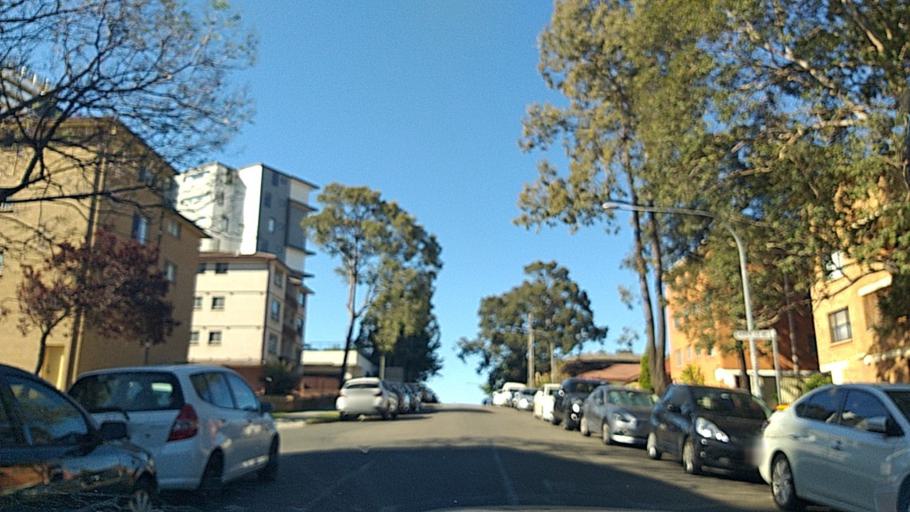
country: AU
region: New South Wales
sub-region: Fairfield
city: Liverpool
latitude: -33.9285
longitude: 150.9198
